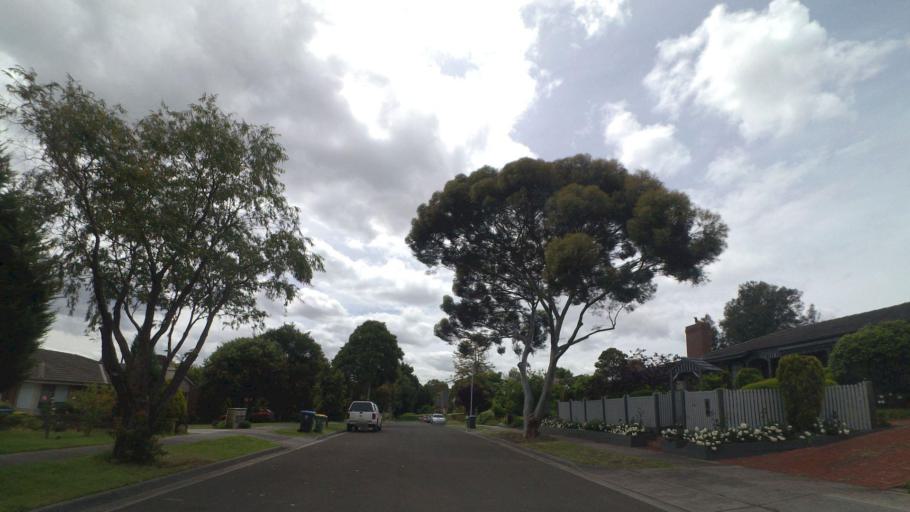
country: AU
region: Victoria
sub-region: Knox
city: Knoxfield
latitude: -37.8764
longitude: 145.2475
